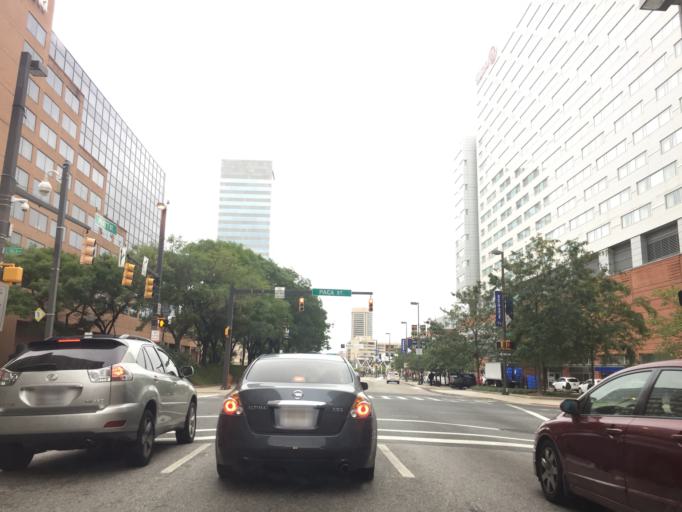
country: US
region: Maryland
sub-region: City of Baltimore
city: Baltimore
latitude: 39.2862
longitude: -76.6224
